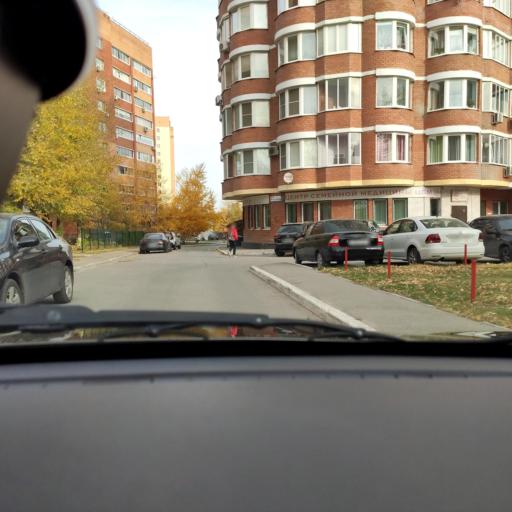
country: RU
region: Samara
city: Tol'yatti
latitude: 53.5372
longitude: 49.3612
